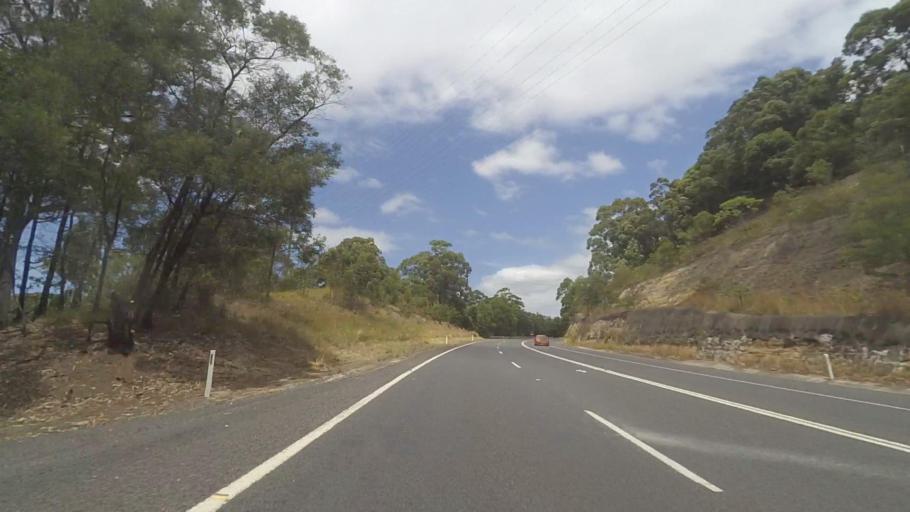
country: AU
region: New South Wales
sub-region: Shoalhaven Shire
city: Milton
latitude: -35.2450
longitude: 150.4256
